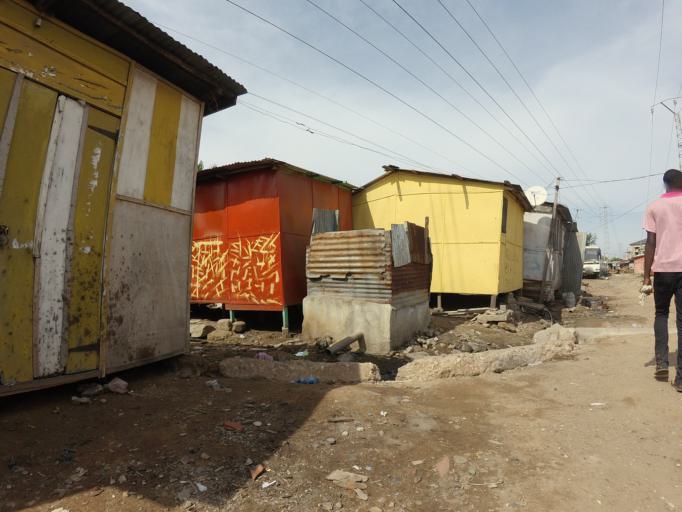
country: GH
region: Greater Accra
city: Dome
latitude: 5.6228
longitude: -0.2311
